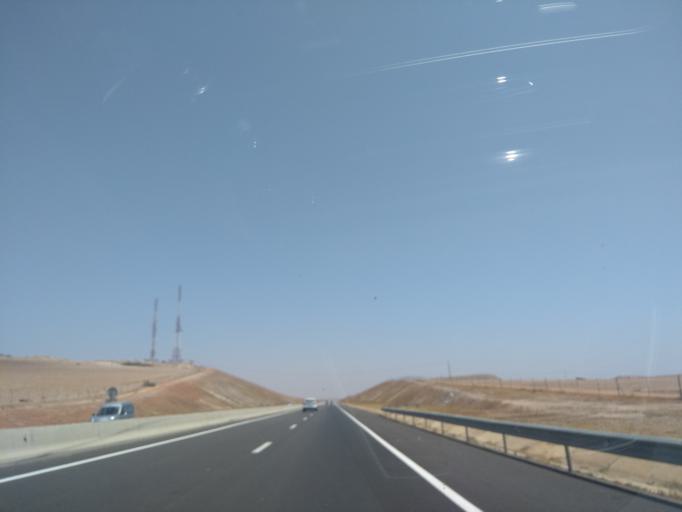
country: MA
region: Marrakech-Tensift-Al Haouz
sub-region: Kelaa-Des-Sraghna
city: Sidi Abdallah
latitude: 32.3072
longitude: -7.9590
